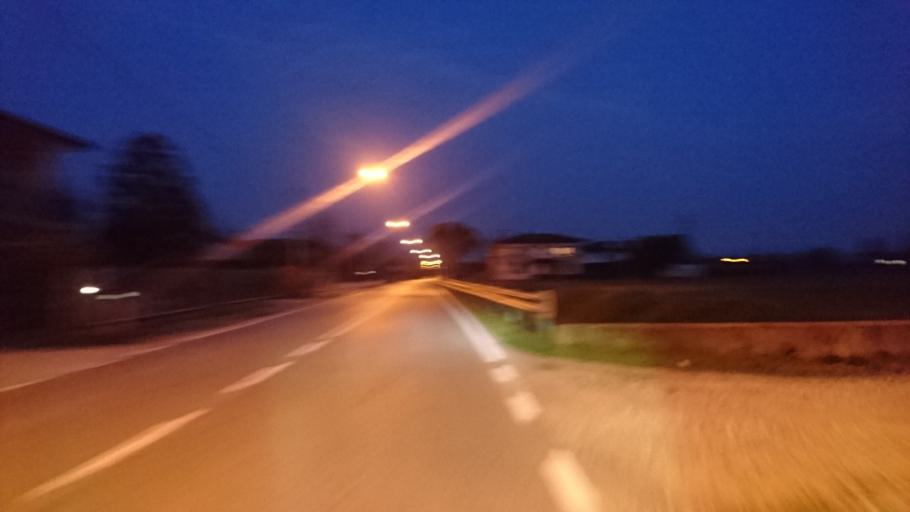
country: IT
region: Veneto
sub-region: Provincia di Padova
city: Abano Terme
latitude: 45.3698
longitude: 11.8039
